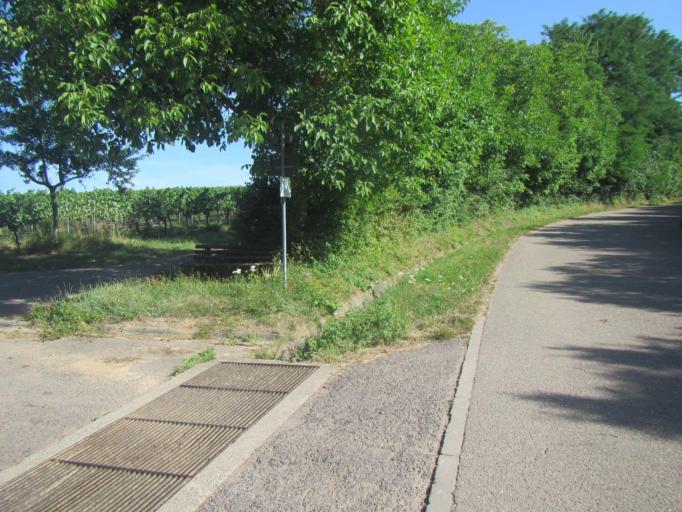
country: DE
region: Rheinland-Pfalz
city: Billigheim-Ingenheim
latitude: 49.1436
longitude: 8.0818
